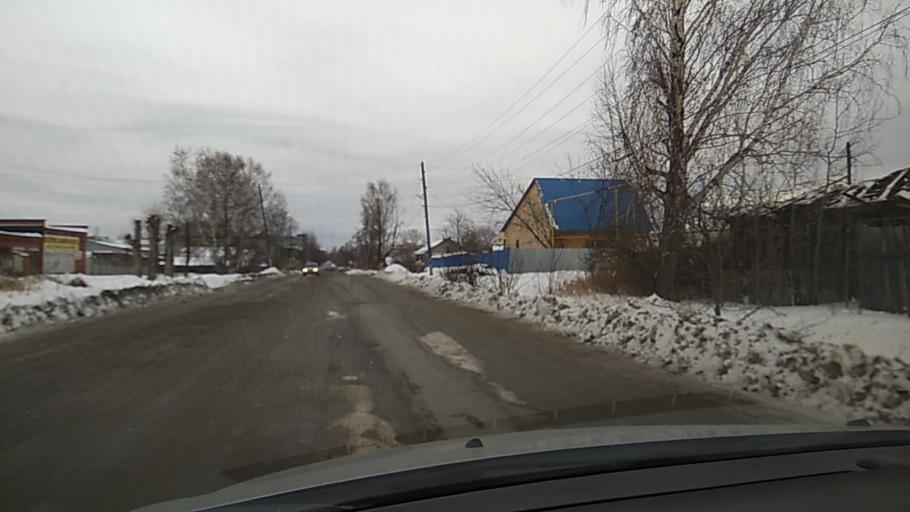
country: RU
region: Sverdlovsk
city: Revda
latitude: 56.8082
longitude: 59.9358
